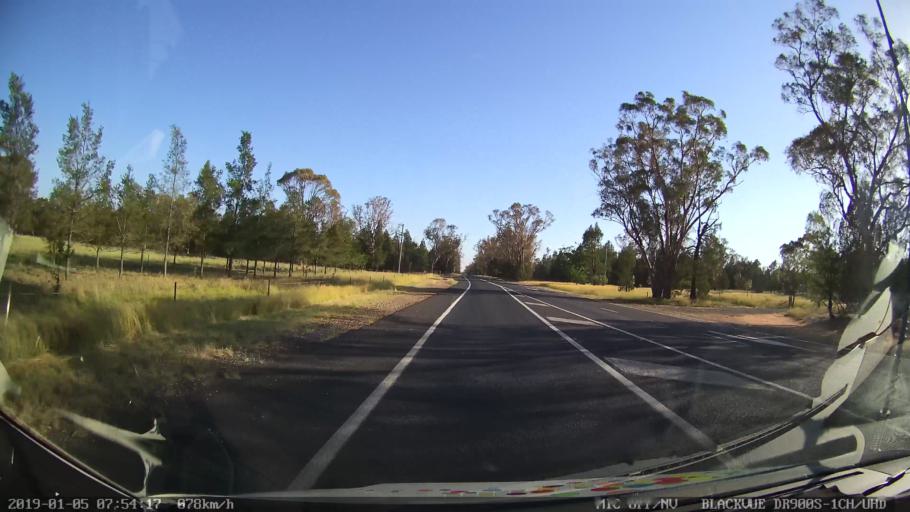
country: AU
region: New South Wales
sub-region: Gilgandra
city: Gilgandra
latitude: -31.7349
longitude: 148.6481
